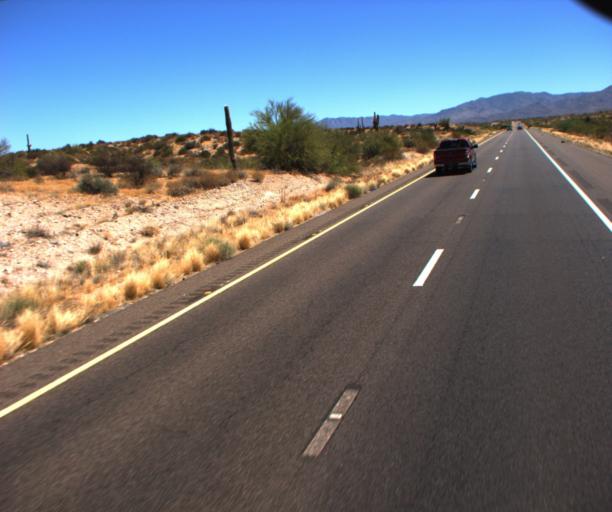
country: US
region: Arizona
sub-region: Maricopa County
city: Rio Verde
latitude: 33.6381
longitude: -111.5438
